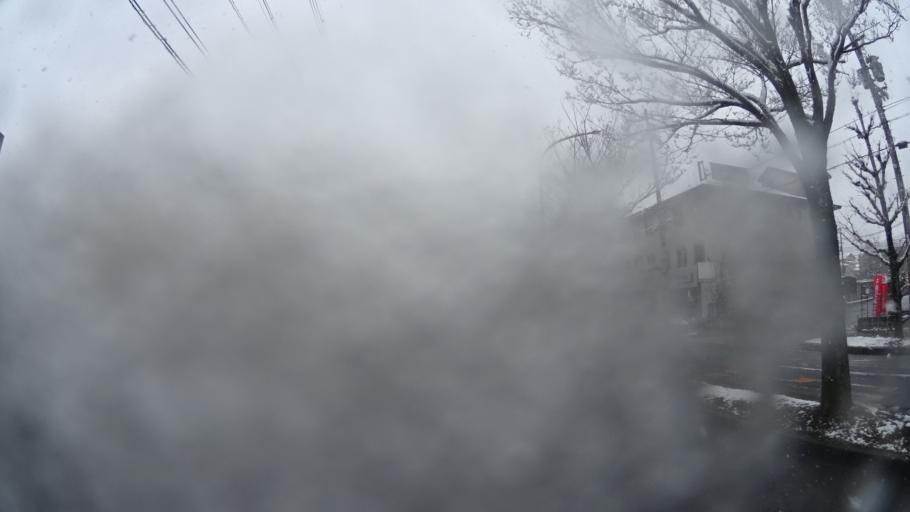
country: JP
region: Kyoto
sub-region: Kyoto-shi
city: Kamigyo-ku
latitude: 35.0639
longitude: 135.7907
